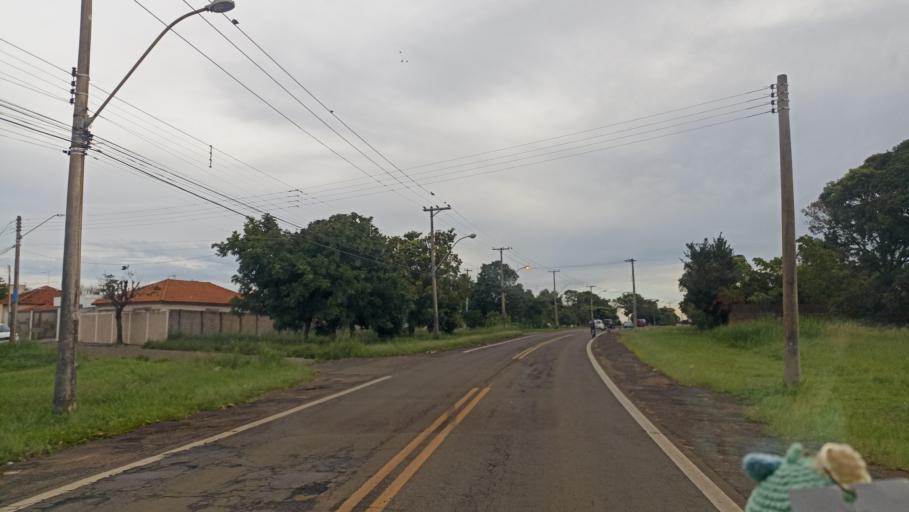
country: BR
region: Sao Paulo
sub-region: Jaboticabal
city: Jaboticabal
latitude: -21.2593
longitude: -48.3296
